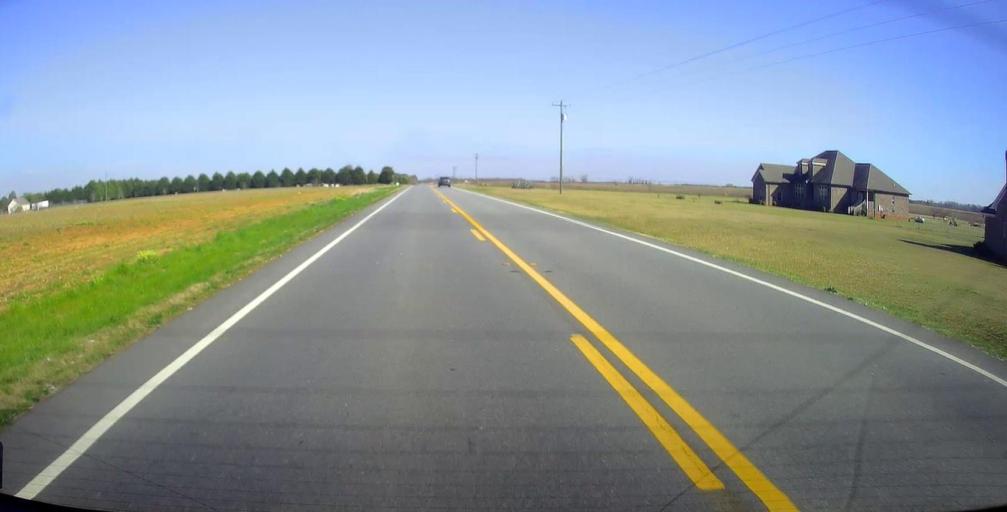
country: US
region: Georgia
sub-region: Dooly County
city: Unadilla
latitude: 32.3379
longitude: -83.8395
